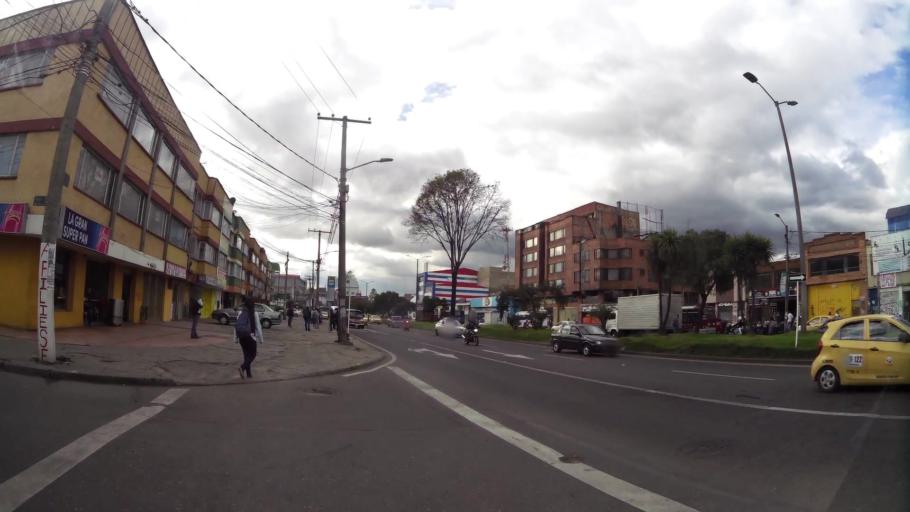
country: CO
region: Bogota D.C.
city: Bogota
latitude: 4.6111
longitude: -74.1322
